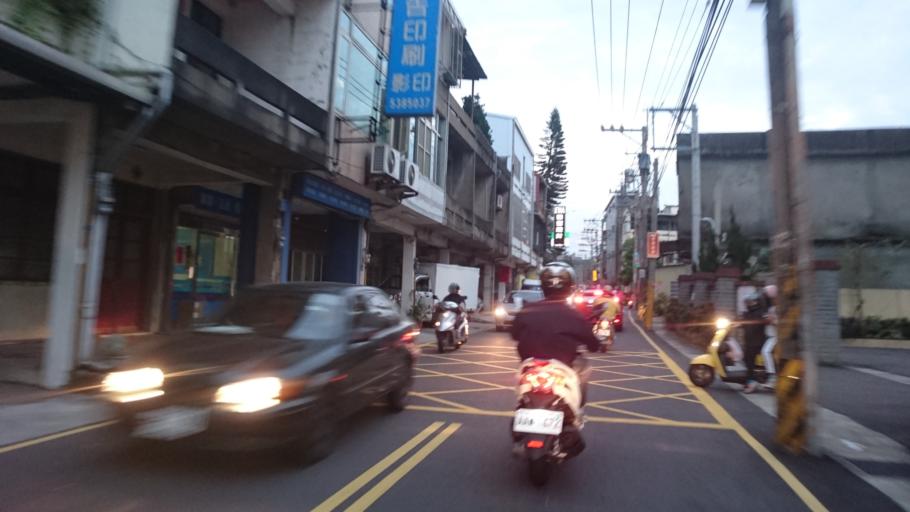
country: TW
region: Taiwan
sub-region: Hsinchu
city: Hsinchu
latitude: 24.7833
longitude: 120.9326
